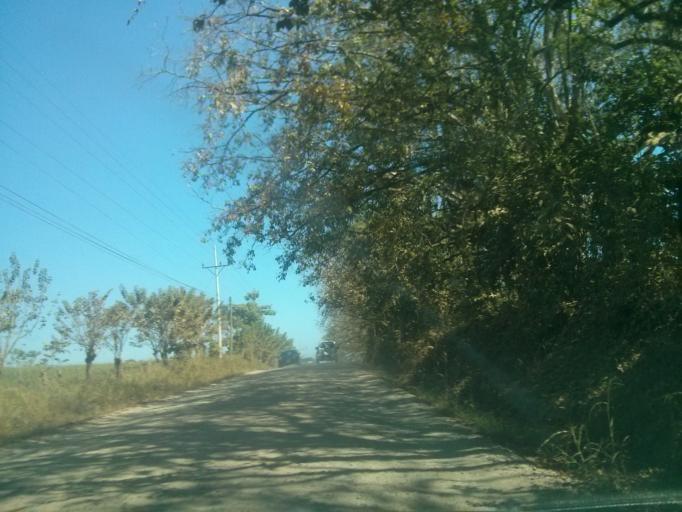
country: CR
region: Puntarenas
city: Paquera
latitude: 9.6666
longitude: -85.1148
